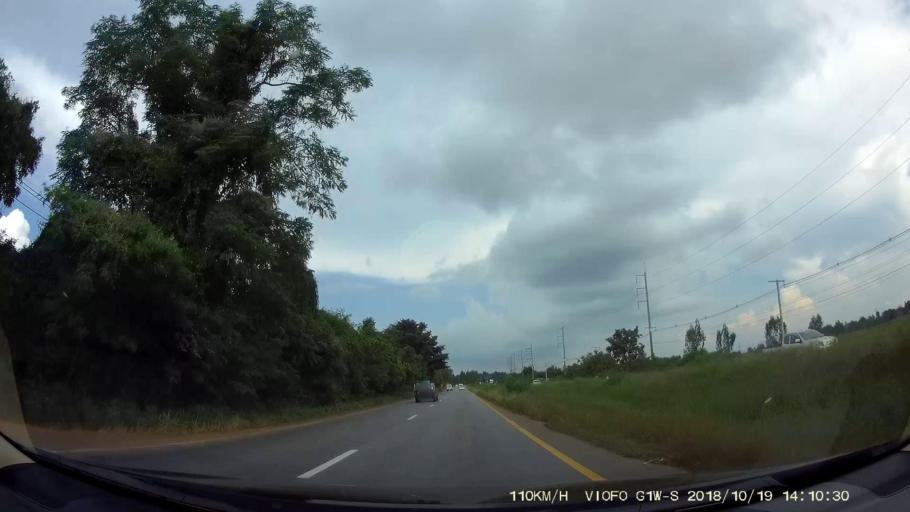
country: TH
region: Chaiyaphum
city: Khon Sawan
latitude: 15.9310
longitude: 102.1471
